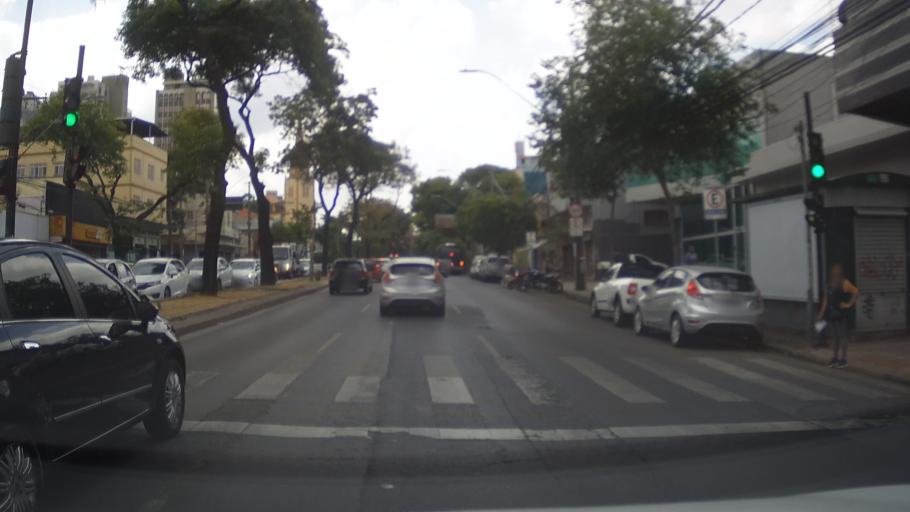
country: BR
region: Minas Gerais
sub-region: Belo Horizonte
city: Belo Horizonte
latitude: -19.9174
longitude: -43.9265
